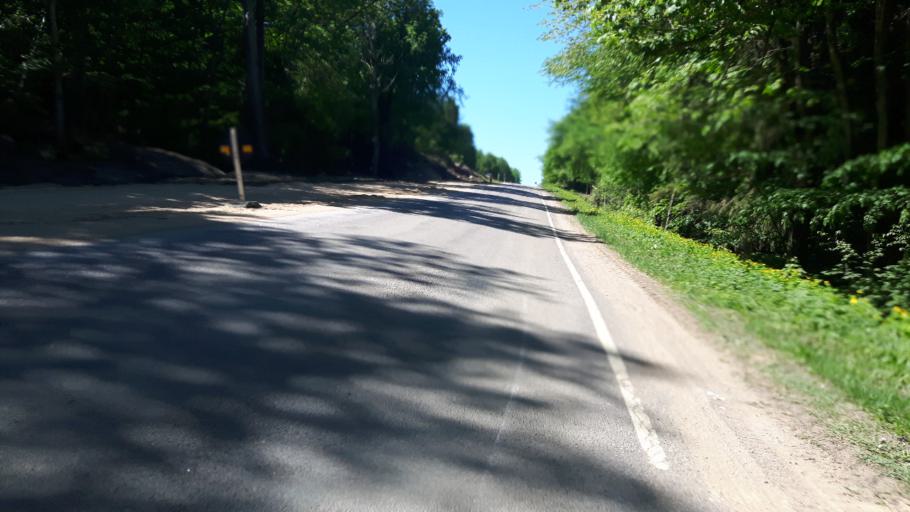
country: EE
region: Ida-Virumaa
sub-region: Narva-Joesuu linn
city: Narva-Joesuu
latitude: 59.4144
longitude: 27.9595
